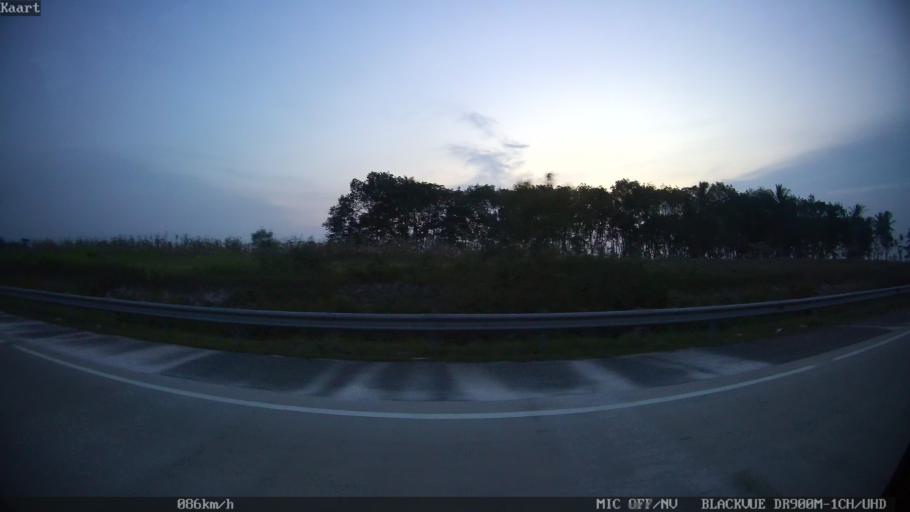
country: ID
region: Lampung
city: Sidorejo
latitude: -5.6197
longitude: 105.5620
